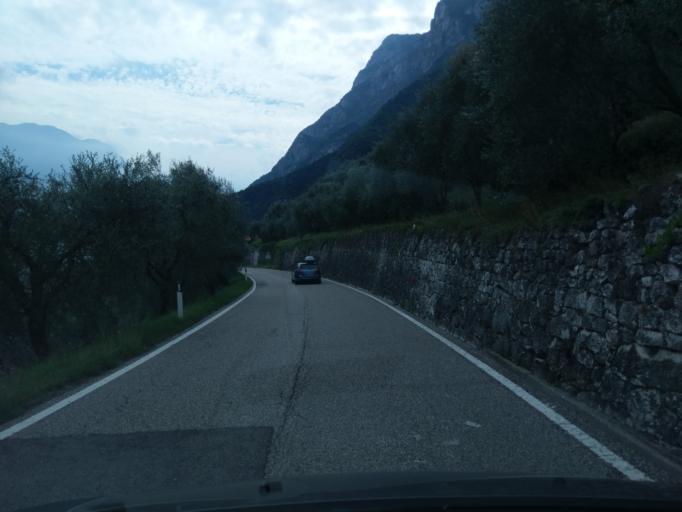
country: IT
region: Trentino-Alto Adige
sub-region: Provincia di Trento
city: Tenno
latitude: 45.9031
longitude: 10.8321
